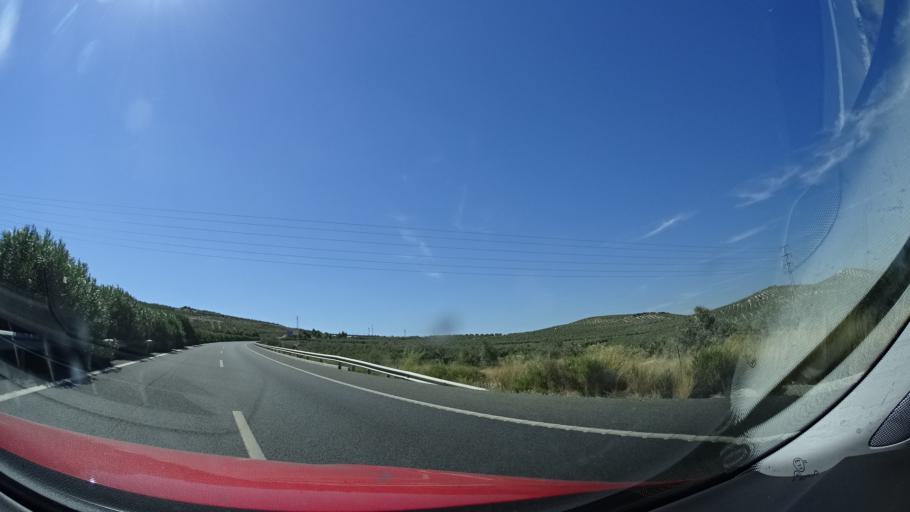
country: ES
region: Andalusia
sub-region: Provincia de Sevilla
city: Estepa
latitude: 37.2960
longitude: -4.8943
